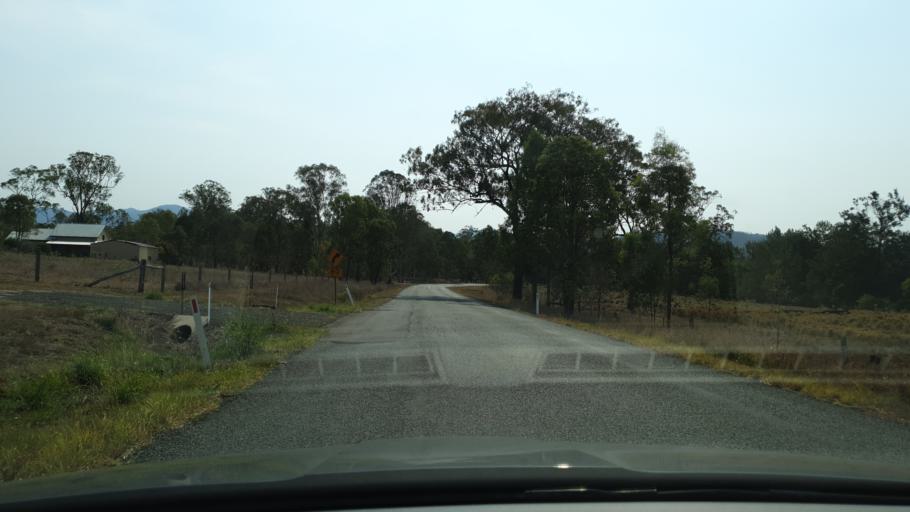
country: AU
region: Queensland
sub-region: Ipswich
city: Deebing Heights
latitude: -28.1380
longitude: 152.5888
